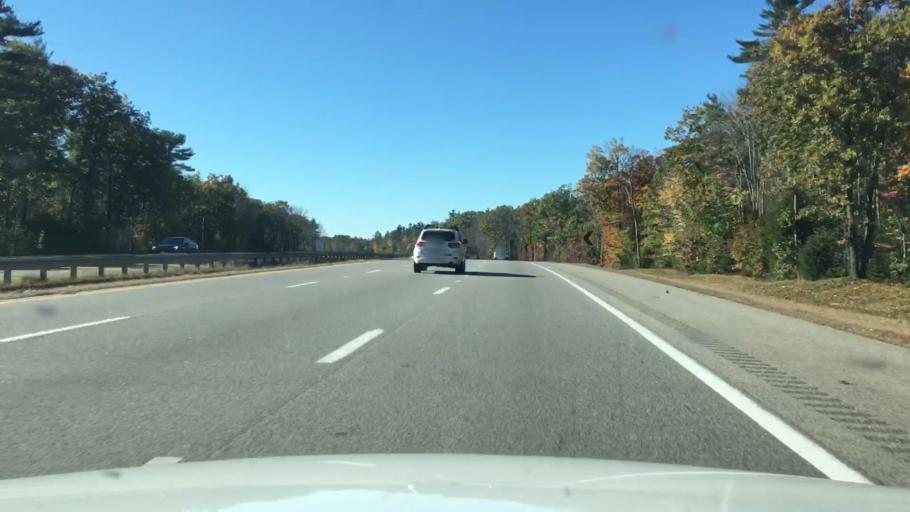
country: US
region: Maine
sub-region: York County
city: Biddeford
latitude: 43.4638
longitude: -70.5217
